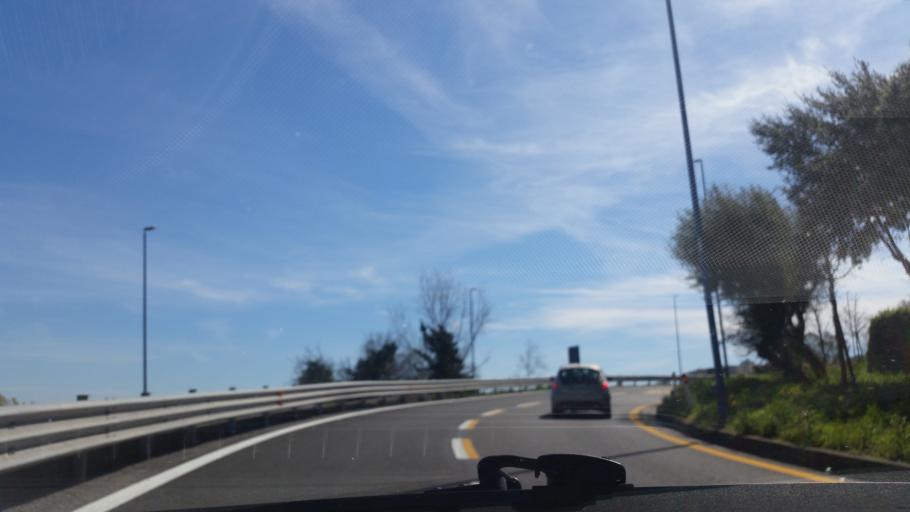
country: IT
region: Campania
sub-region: Provincia di Napoli
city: Napoli
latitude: 40.8595
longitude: 14.2338
